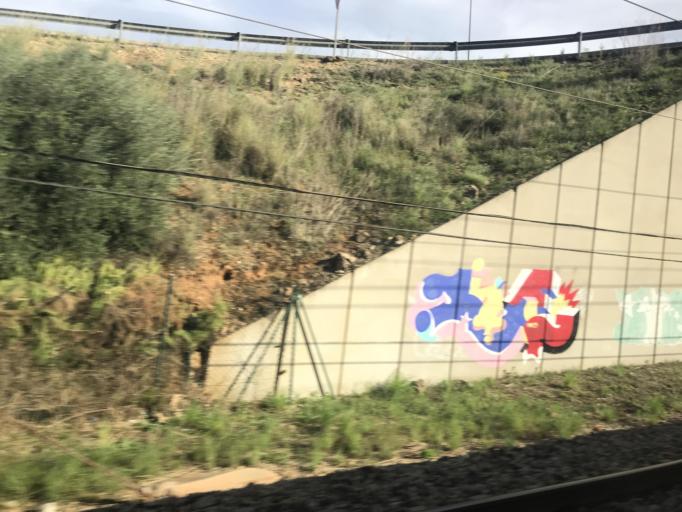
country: ES
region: Valencia
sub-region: Provincia de Castello
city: Alcala de Xivert
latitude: 40.3129
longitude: 0.2320
